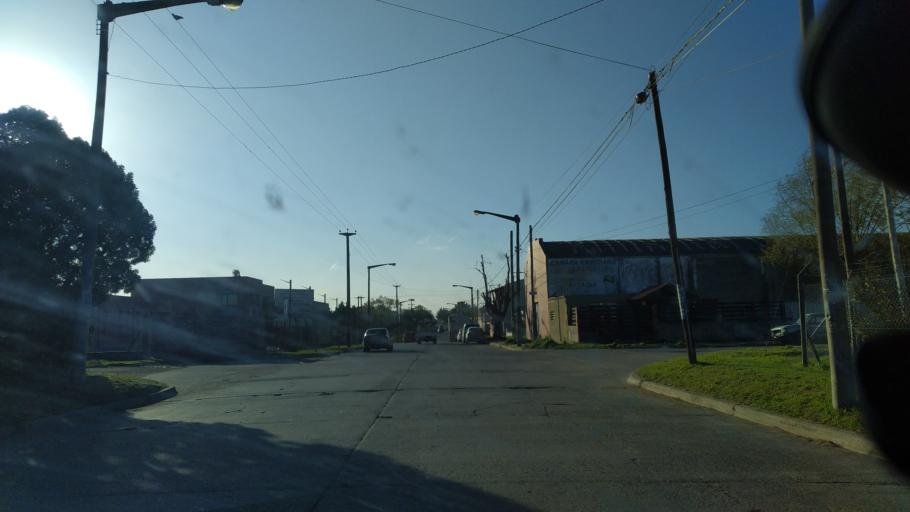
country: AR
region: Buenos Aires
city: Necochea
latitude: -38.5625
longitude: -58.7101
